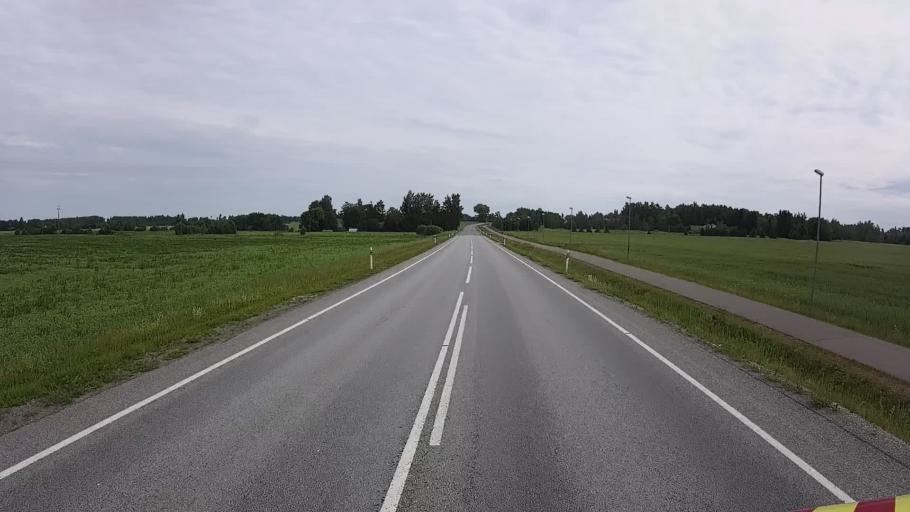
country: EE
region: Viljandimaa
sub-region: Karksi vald
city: Karksi-Nuia
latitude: 58.1116
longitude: 25.5702
